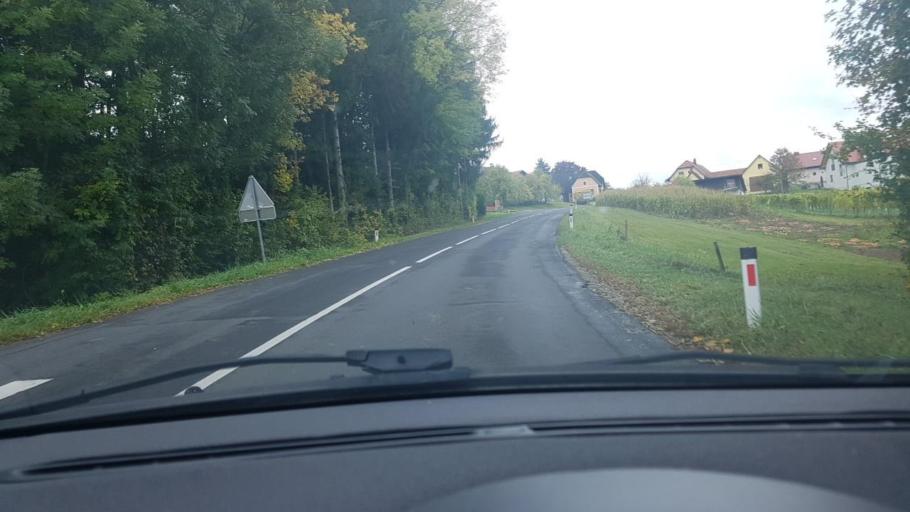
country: AT
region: Styria
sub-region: Politischer Bezirk Leibnitz
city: Spielfeld
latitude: 46.6985
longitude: 15.6121
